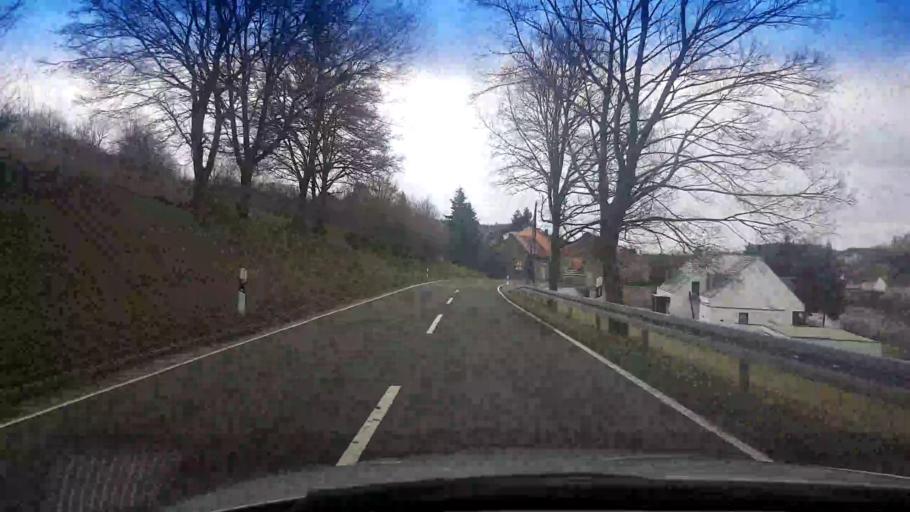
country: DE
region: Bavaria
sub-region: Regierungsbezirk Unterfranken
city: Eltmann
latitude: 49.9329
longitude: 10.6480
